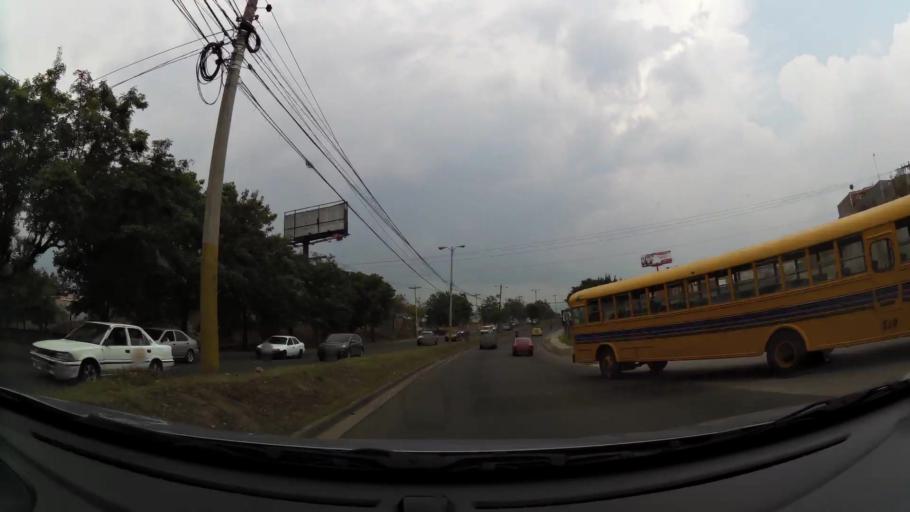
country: HN
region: Francisco Morazan
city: Tegucigalpa
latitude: 14.0762
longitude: -87.1983
